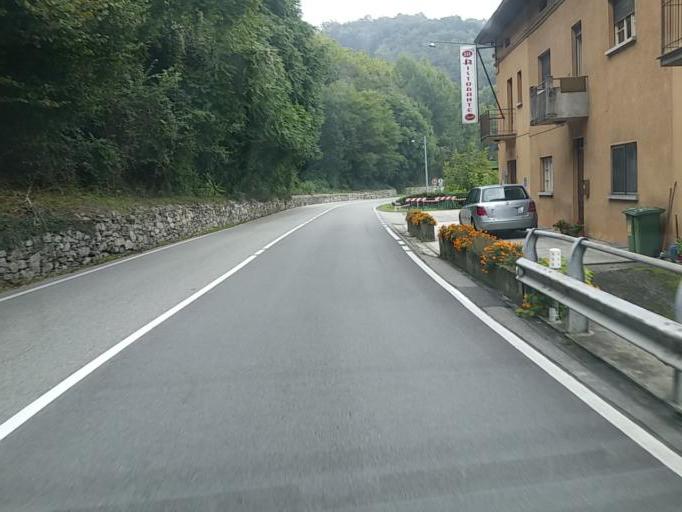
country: IT
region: Piedmont
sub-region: Provincia di Novara
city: Bolzano Novarese
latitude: 45.7699
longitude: 8.4266
